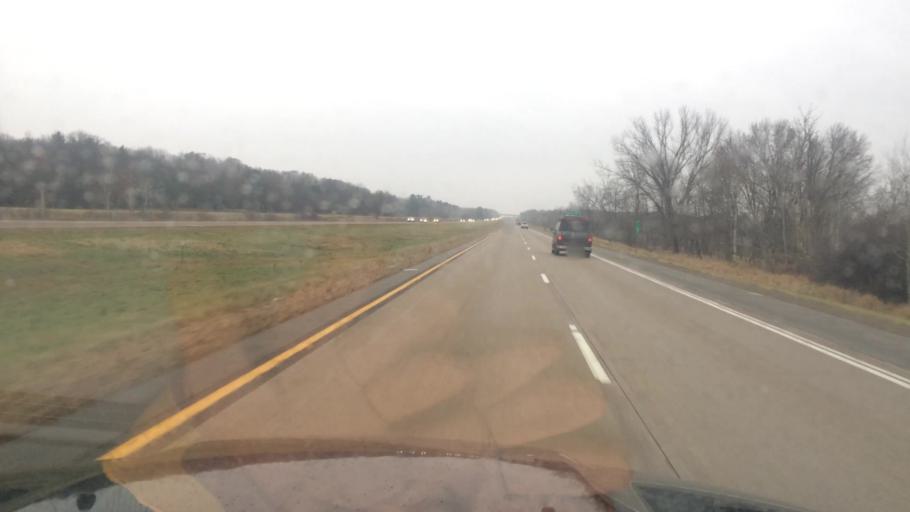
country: US
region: Wisconsin
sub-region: Portage County
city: Stevens Point
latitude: 44.6178
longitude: -89.6272
